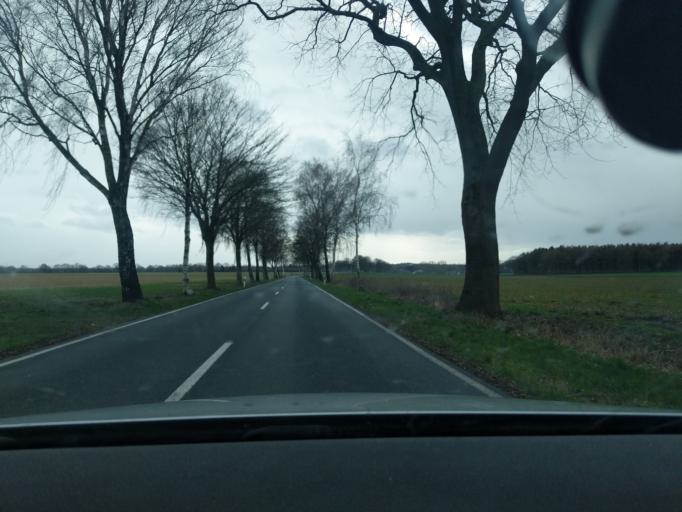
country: DE
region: Lower Saxony
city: Bliedersdorf
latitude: 53.4952
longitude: 9.5317
